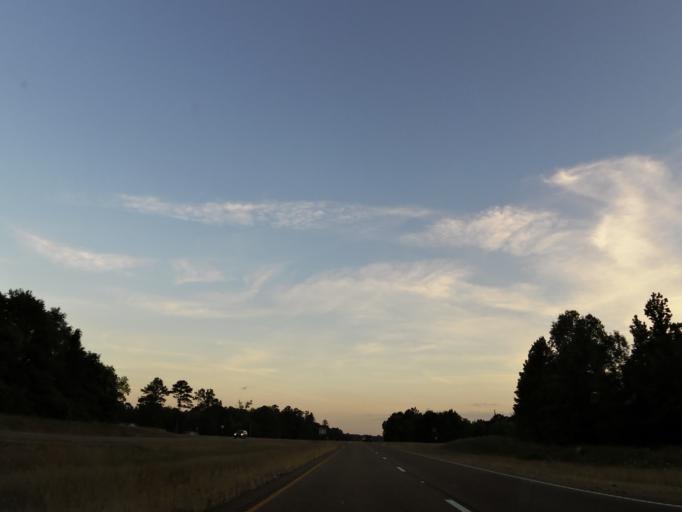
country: US
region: Mississippi
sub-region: Noxubee County
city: Macon
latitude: 32.9852
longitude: -88.5560
